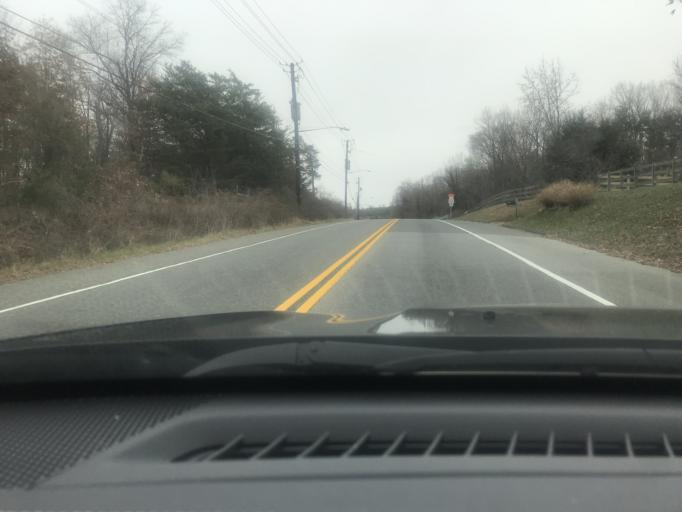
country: US
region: Maryland
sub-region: Prince George's County
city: Friendly
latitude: 38.7784
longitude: -76.9761
